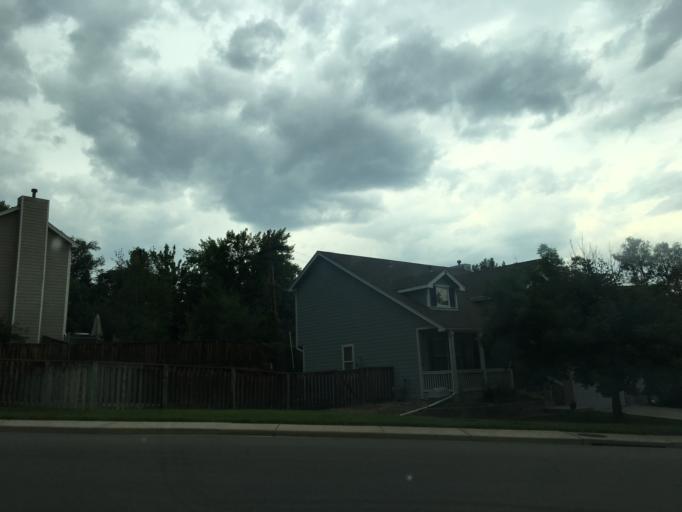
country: US
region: Colorado
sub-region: Arapahoe County
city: Sheridan
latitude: 39.6567
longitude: -105.0343
